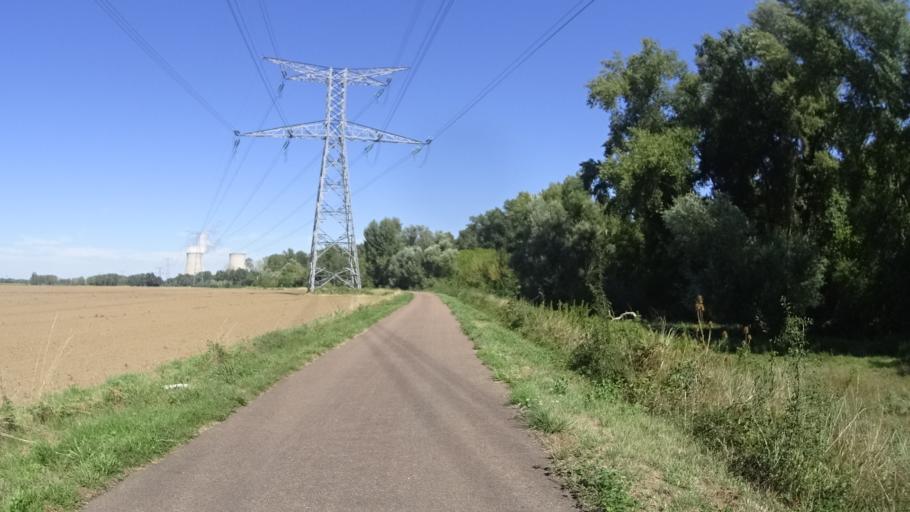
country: FR
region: Centre
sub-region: Departement du Cher
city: Lere
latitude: 47.4904
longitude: 2.8928
